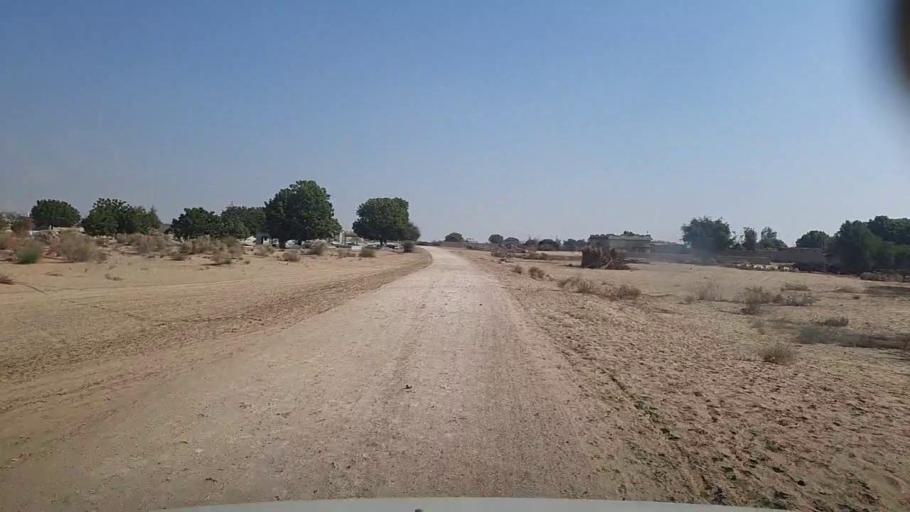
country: PK
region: Sindh
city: Khairpur
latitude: 28.0035
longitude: 69.8524
